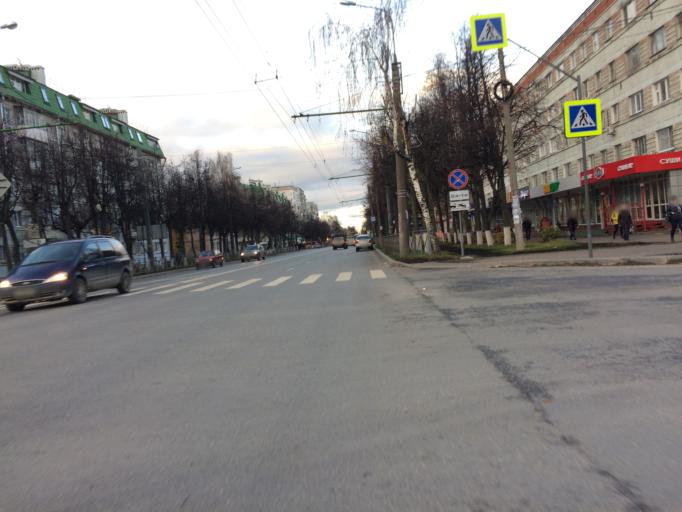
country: RU
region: Mariy-El
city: Yoshkar-Ola
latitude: 56.6398
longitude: 47.8884
